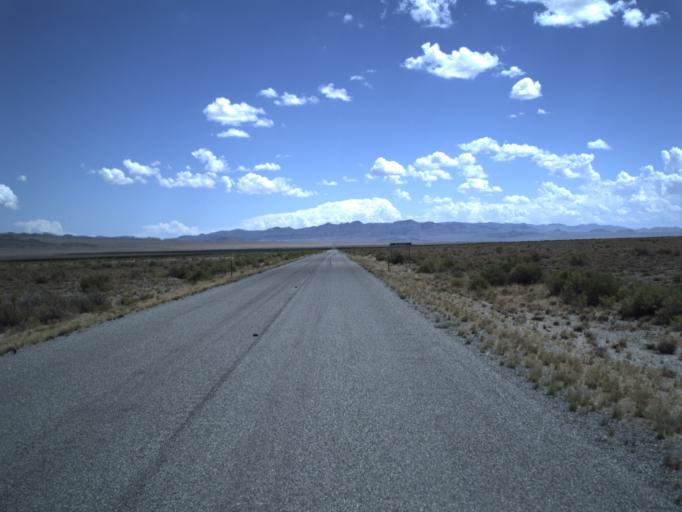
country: US
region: Nevada
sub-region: White Pine County
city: McGill
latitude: 39.0507
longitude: -113.9655
